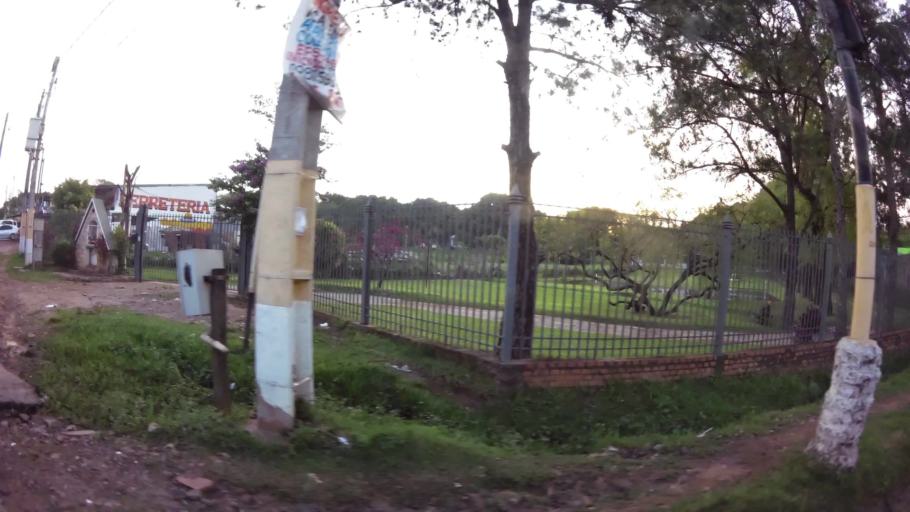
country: PY
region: Central
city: San Lorenzo
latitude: -25.3523
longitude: -57.4907
